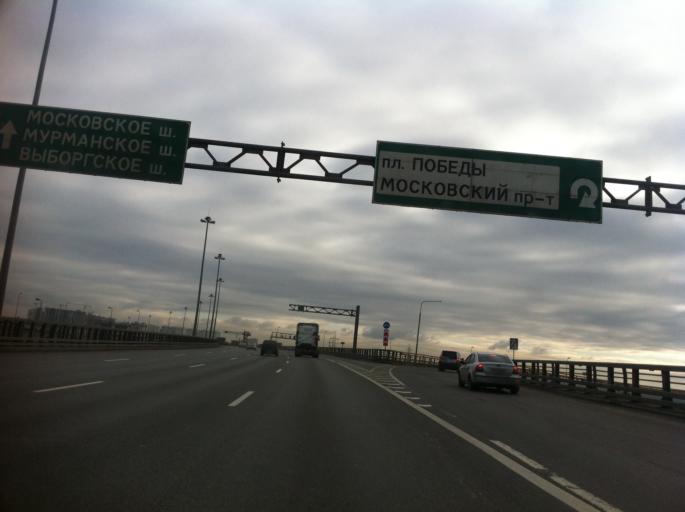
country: RU
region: St.-Petersburg
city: Kupchino
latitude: 59.8105
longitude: 30.3252
